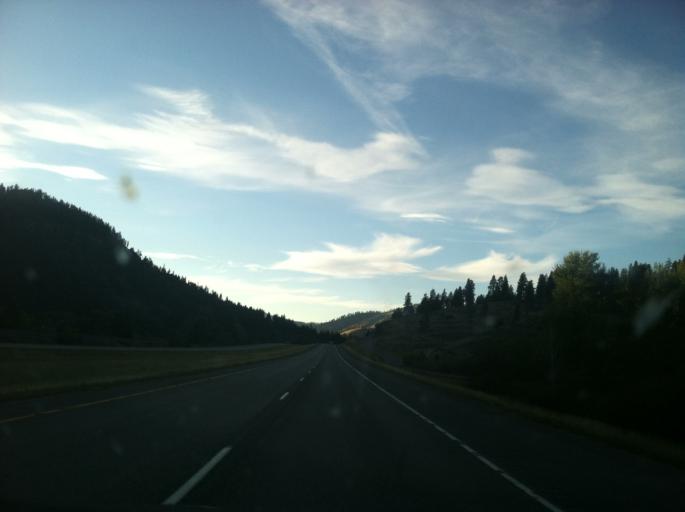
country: US
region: Montana
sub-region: Missoula County
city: Clinton
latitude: 46.7017
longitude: -113.4965
